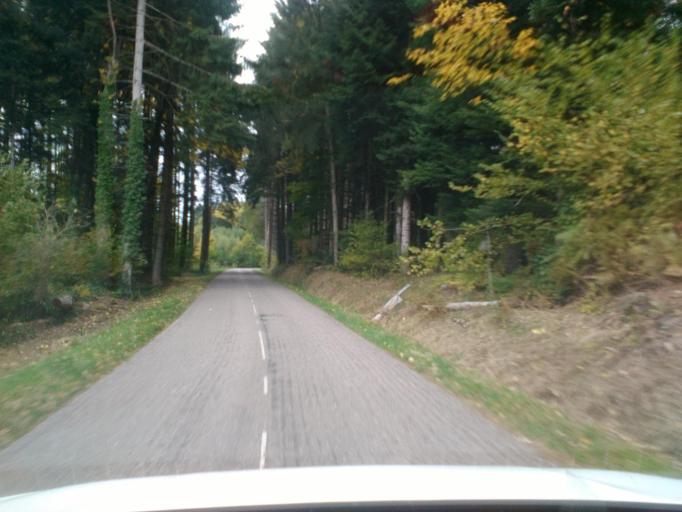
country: FR
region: Lorraine
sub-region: Departement des Vosges
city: Sainte-Marguerite
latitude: 48.3279
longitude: 7.0234
